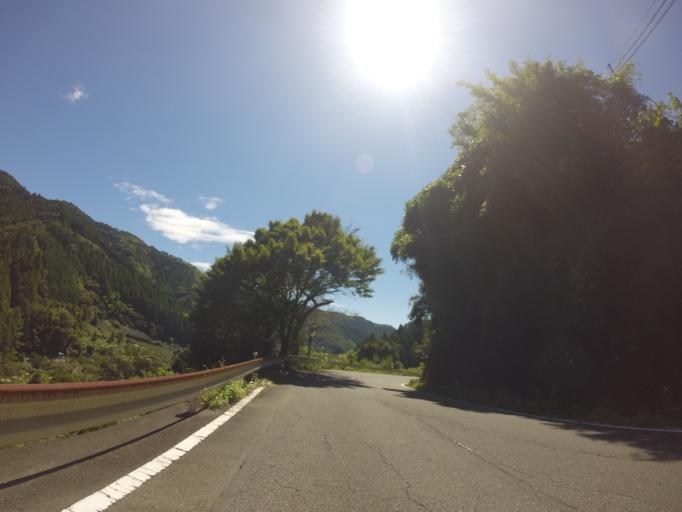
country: JP
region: Shizuoka
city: Fujieda
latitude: 34.9731
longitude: 138.2112
